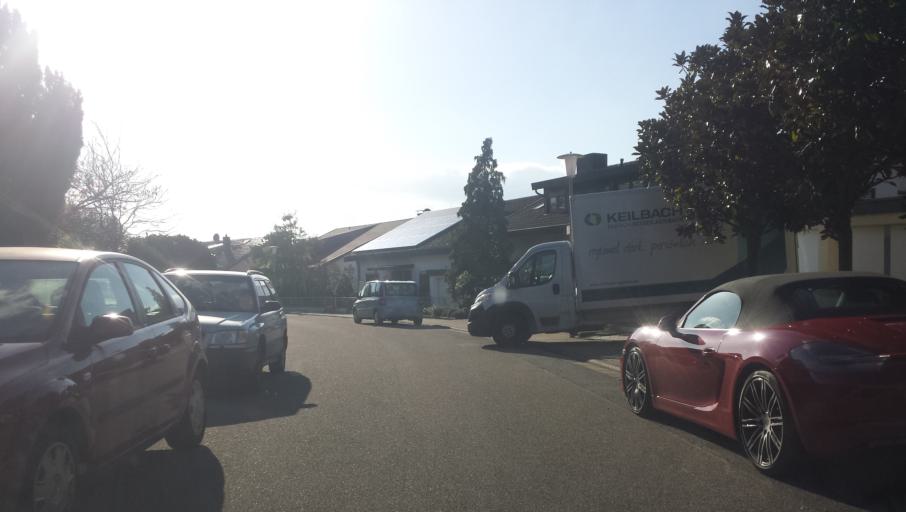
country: DE
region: Baden-Wuerttemberg
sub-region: Karlsruhe Region
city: Malsch
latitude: 49.2395
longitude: 8.7026
